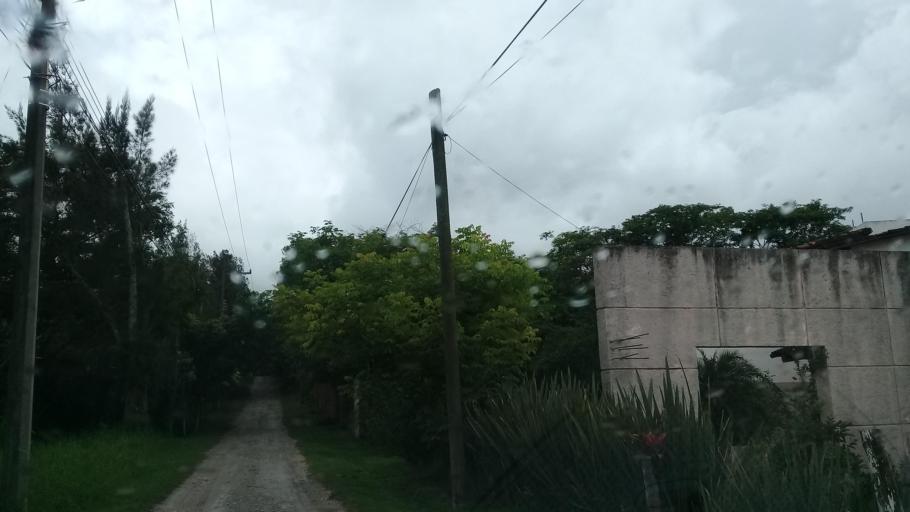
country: MX
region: Veracruz
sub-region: Emiliano Zapata
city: Jacarandas
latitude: 19.5080
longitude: -96.8405
